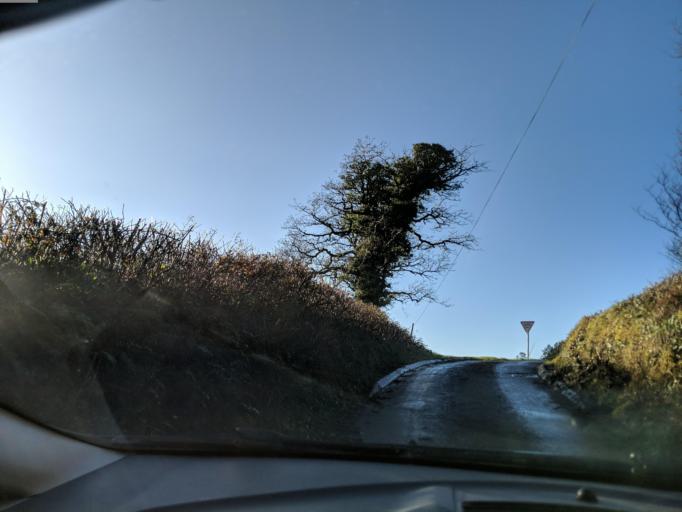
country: GB
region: England
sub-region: Devon
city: Okehampton
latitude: 50.6984
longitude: -4.0829
